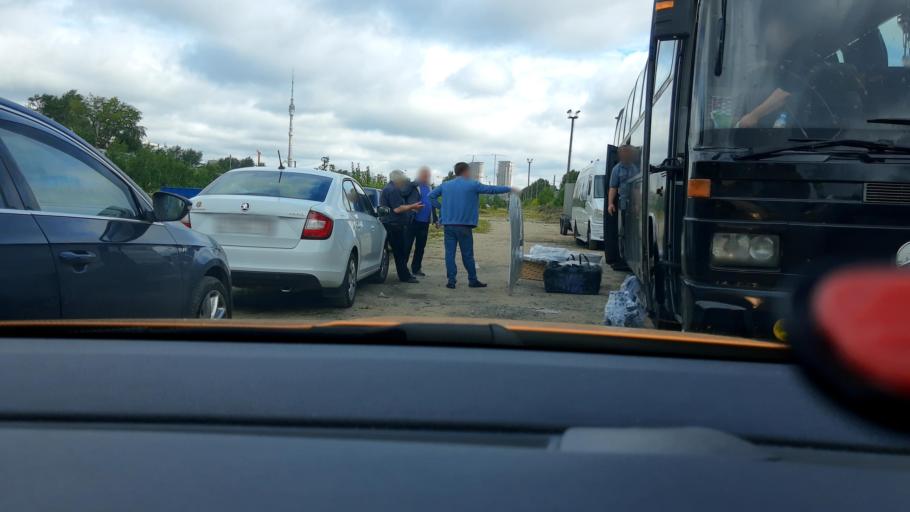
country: RU
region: Moscow
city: Mar'ina Roshcha
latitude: 55.7941
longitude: 37.6286
